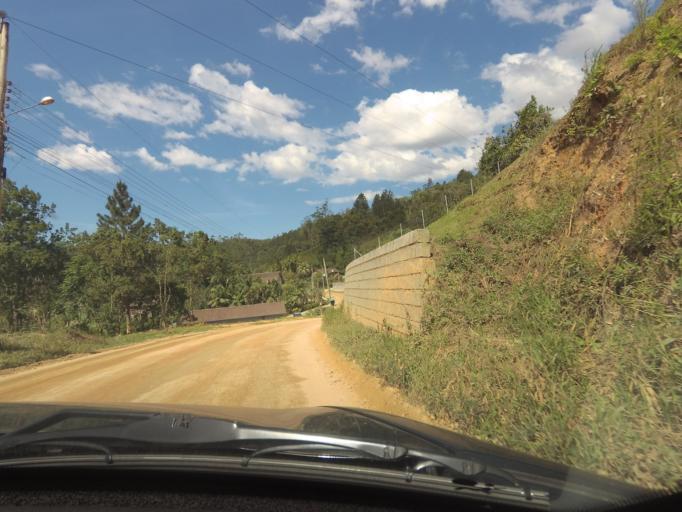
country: BR
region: Santa Catarina
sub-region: Brusque
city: Brusque
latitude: -27.0676
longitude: -48.9527
